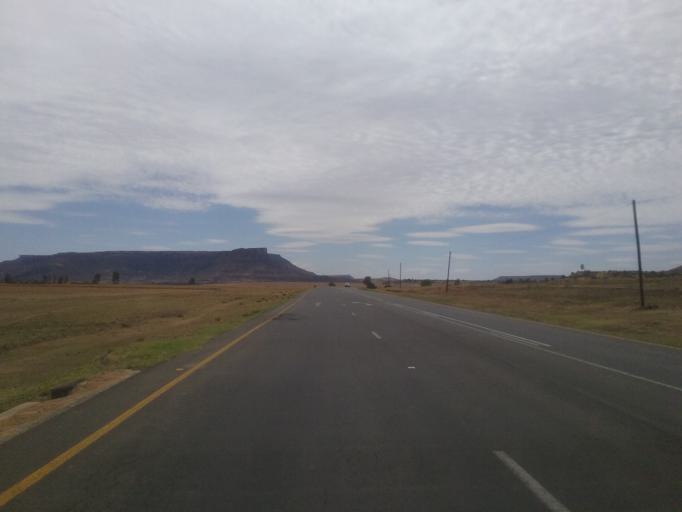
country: LS
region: Mafeteng
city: Mafeteng
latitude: -29.6815
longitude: 27.4449
